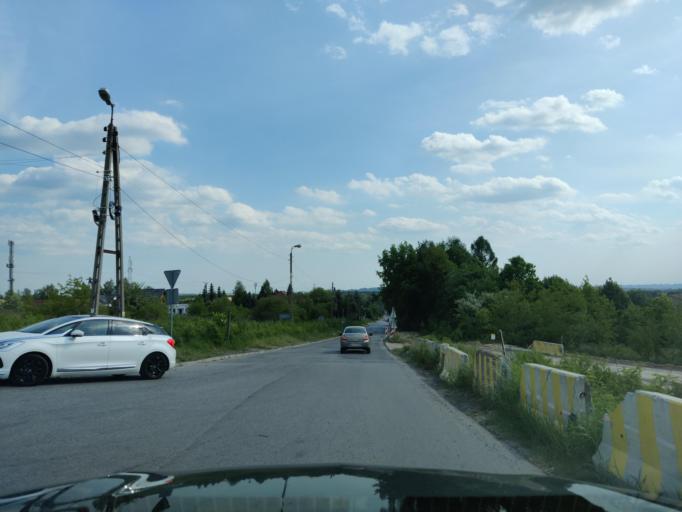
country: PL
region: Silesian Voivodeship
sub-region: Dabrowa Gornicza
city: Dabrowa Gornicza
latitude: 50.3857
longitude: 19.2420
